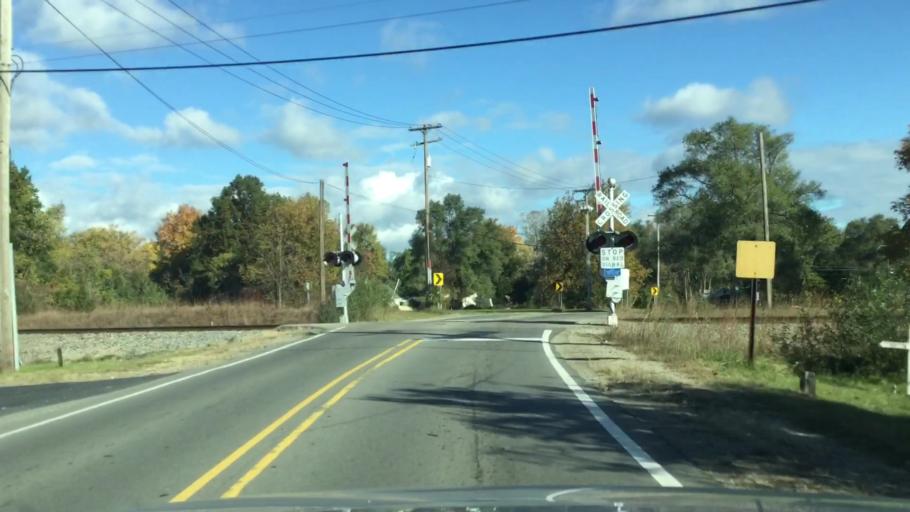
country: US
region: Michigan
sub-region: Oakland County
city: Waterford
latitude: 42.6816
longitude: -83.3816
